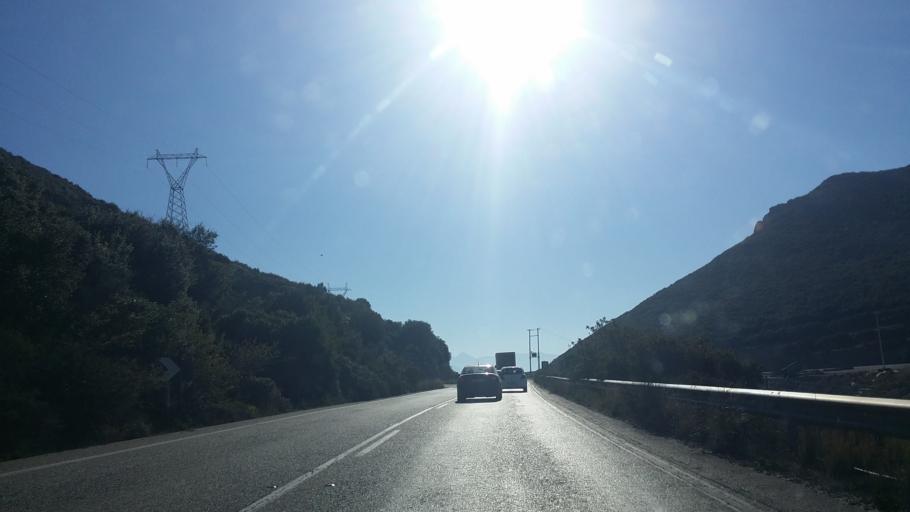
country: GR
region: West Greece
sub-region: Nomos Aitolias kai Akarnanias
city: Galatas
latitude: 38.3618
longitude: 21.6580
